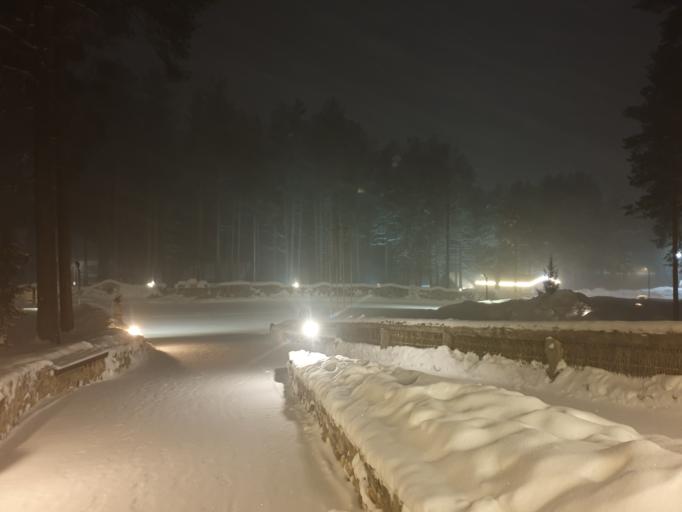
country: RU
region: Republic of Karelia
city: Medvezh'yegorsk
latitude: 62.9143
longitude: 34.5137
